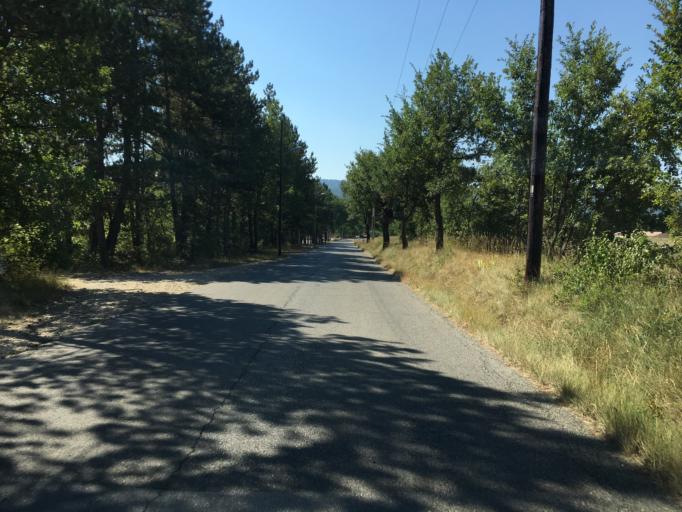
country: FR
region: Provence-Alpes-Cote d'Azur
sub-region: Departement des Alpes-de-Haute-Provence
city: Mallemoisson
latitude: 44.0538
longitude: 6.1487
